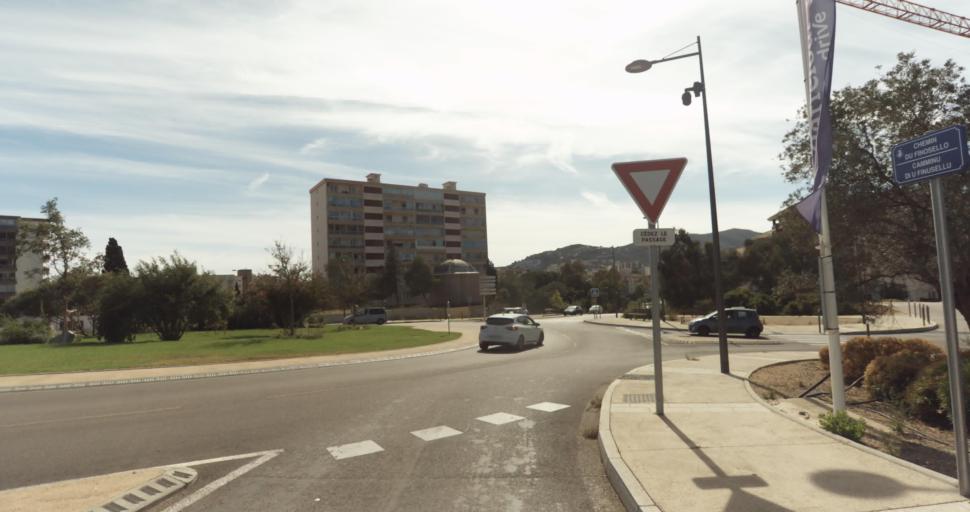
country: FR
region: Corsica
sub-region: Departement de la Corse-du-Sud
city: Ajaccio
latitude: 41.9413
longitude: 8.7460
